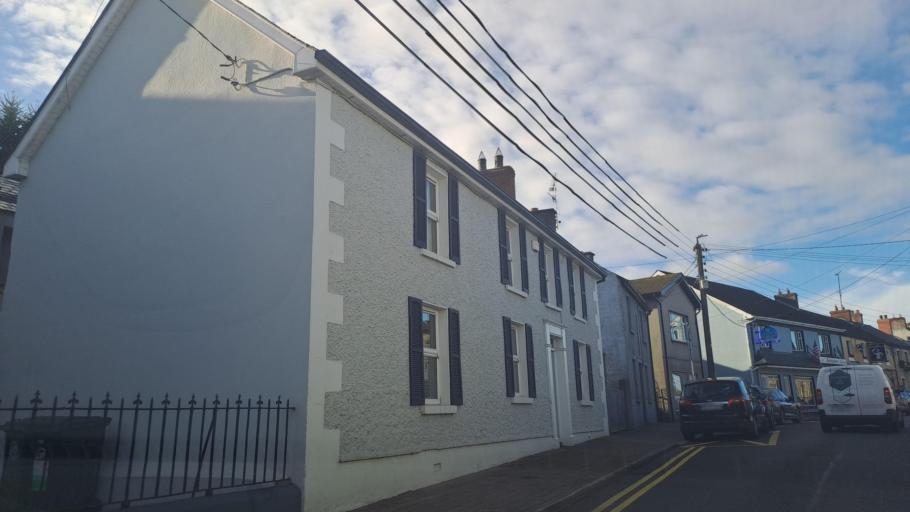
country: IE
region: Ulster
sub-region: County Monaghan
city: Carrickmacross
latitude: 53.9753
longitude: -6.7162
